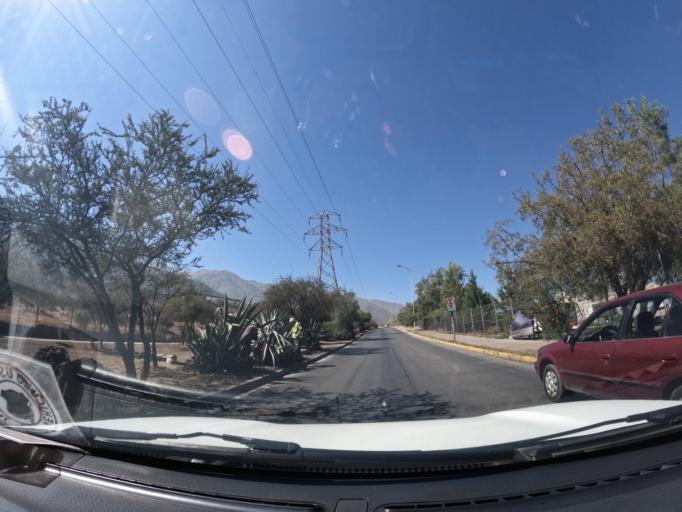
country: CL
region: Santiago Metropolitan
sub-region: Provincia de Santiago
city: Villa Presidente Frei, Nunoa, Santiago, Chile
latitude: -33.4829
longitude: -70.5228
